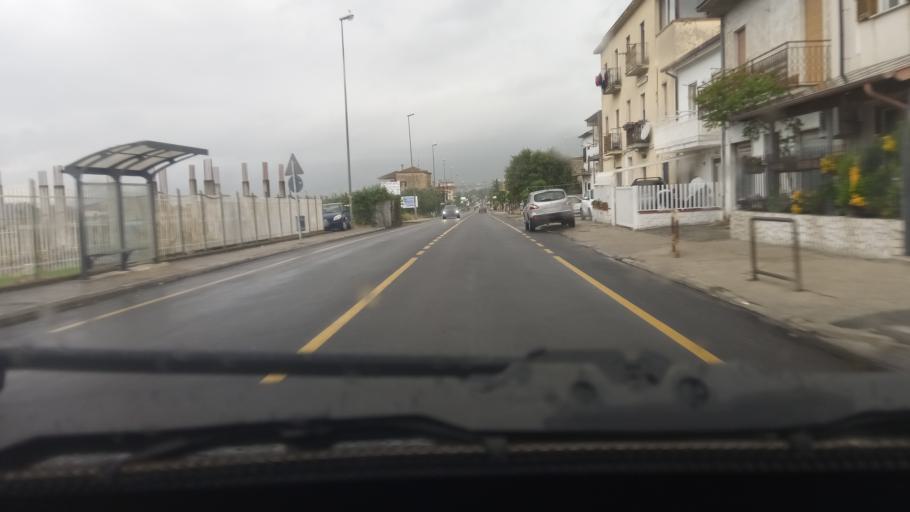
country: IT
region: Latium
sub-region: Provincia di Latina
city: Penitro
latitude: 41.2602
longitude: 13.6925
